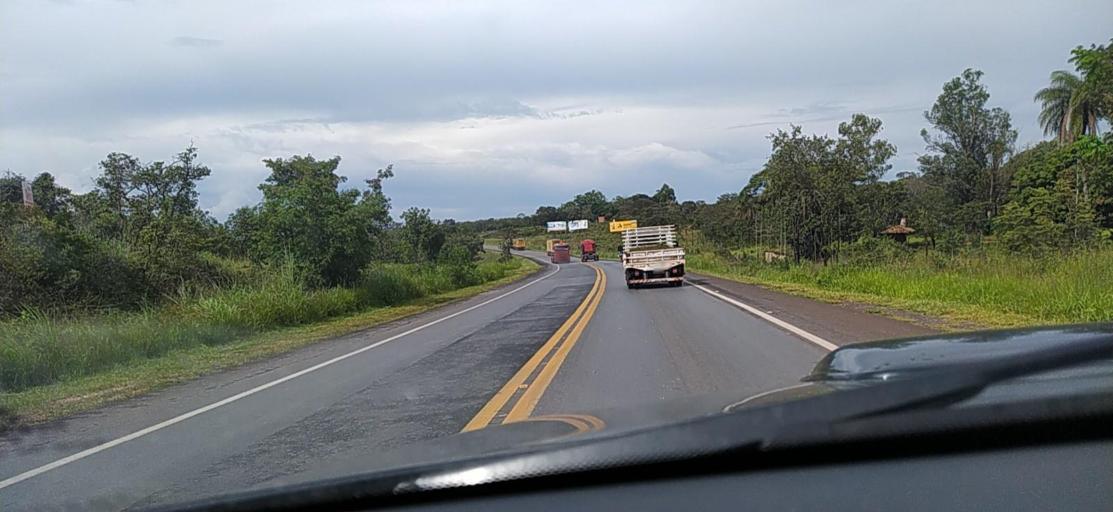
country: BR
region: Minas Gerais
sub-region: Montes Claros
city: Montes Claros
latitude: -16.8718
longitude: -43.8562
